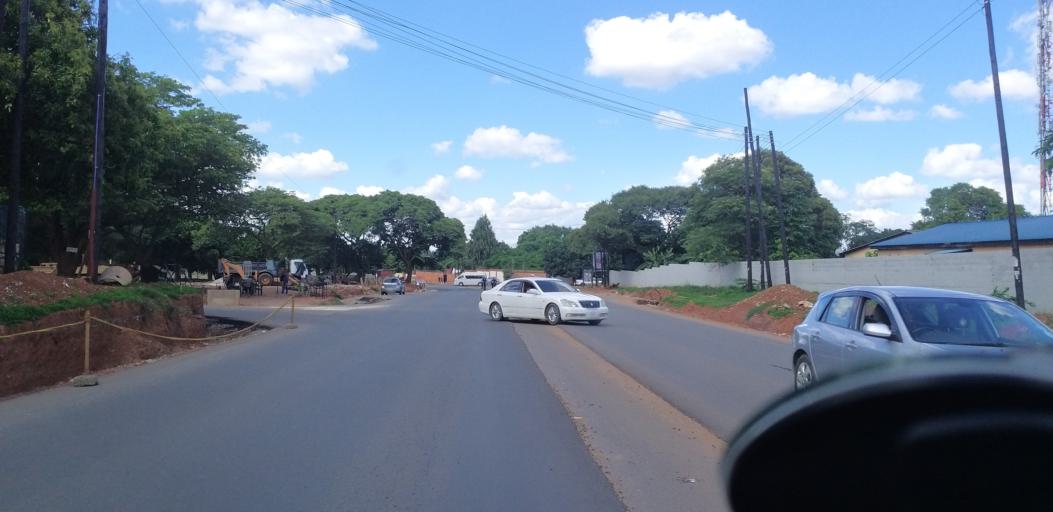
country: ZM
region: Lusaka
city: Lusaka
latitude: -15.4307
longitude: 28.3417
